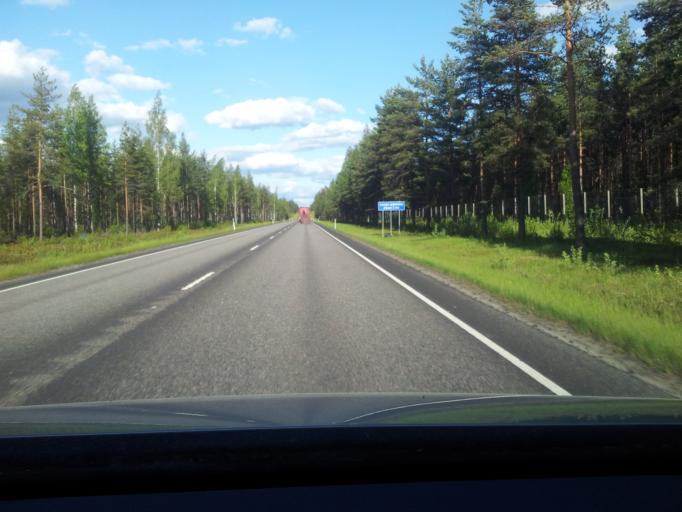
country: FI
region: Kymenlaakso
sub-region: Kouvola
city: Kouvola
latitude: 60.9041
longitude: 26.9421
